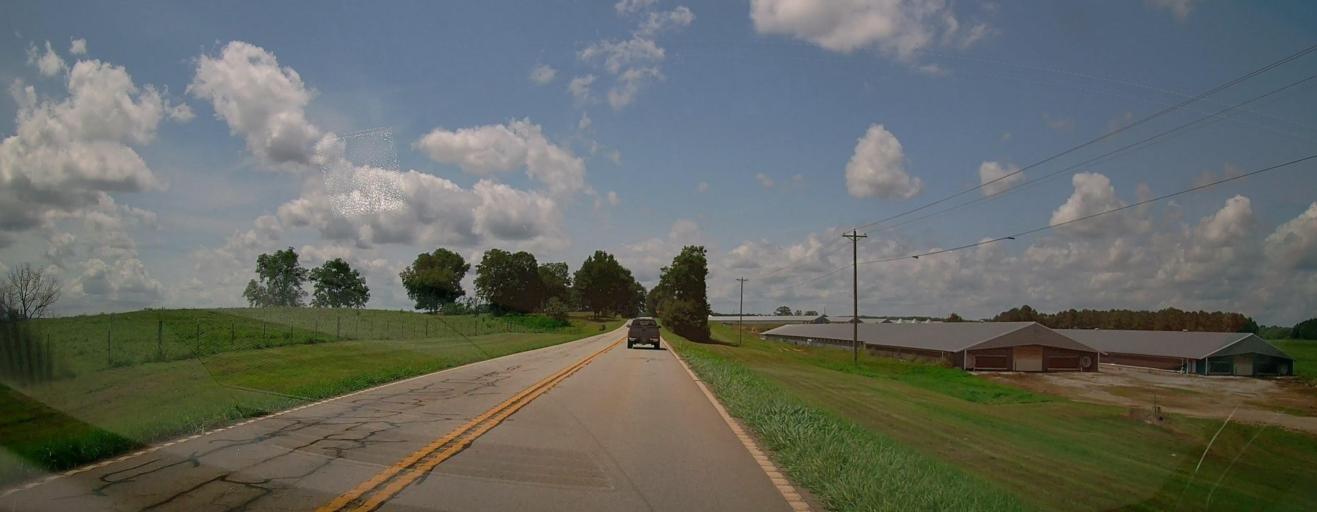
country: US
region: Georgia
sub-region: Heard County
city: Franklin
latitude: 33.3621
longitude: -85.2223
